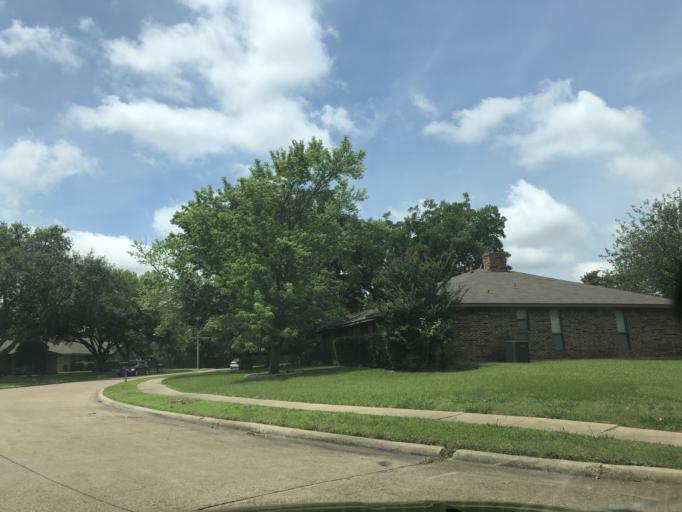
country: US
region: Texas
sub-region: Dallas County
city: Garland
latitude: 32.8515
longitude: -96.6218
